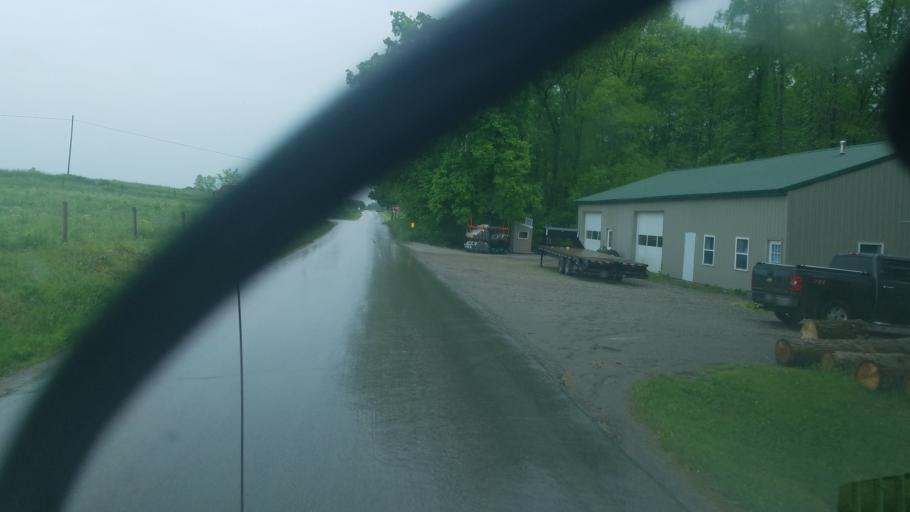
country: US
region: Ohio
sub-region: Wayne County
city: Apple Creek
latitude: 40.7009
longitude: -81.8425
